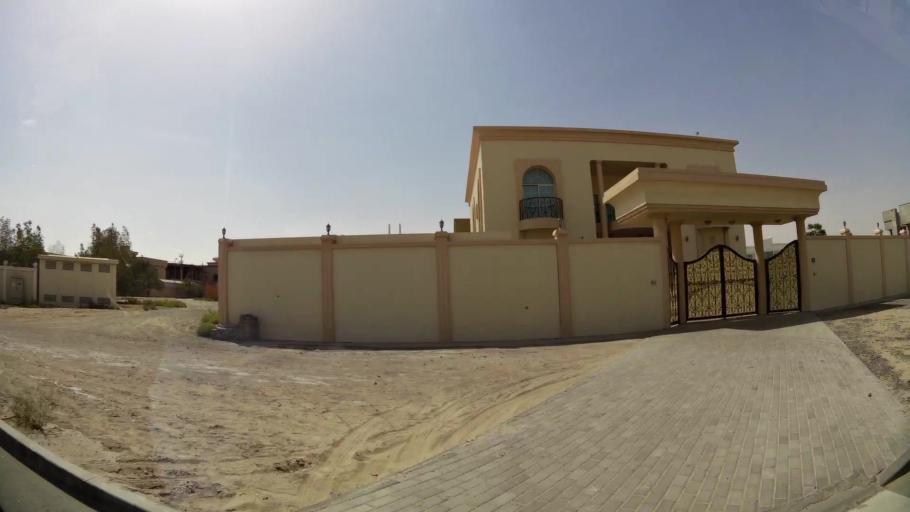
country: AE
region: Ash Shariqah
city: Sharjah
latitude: 25.1994
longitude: 55.4250
